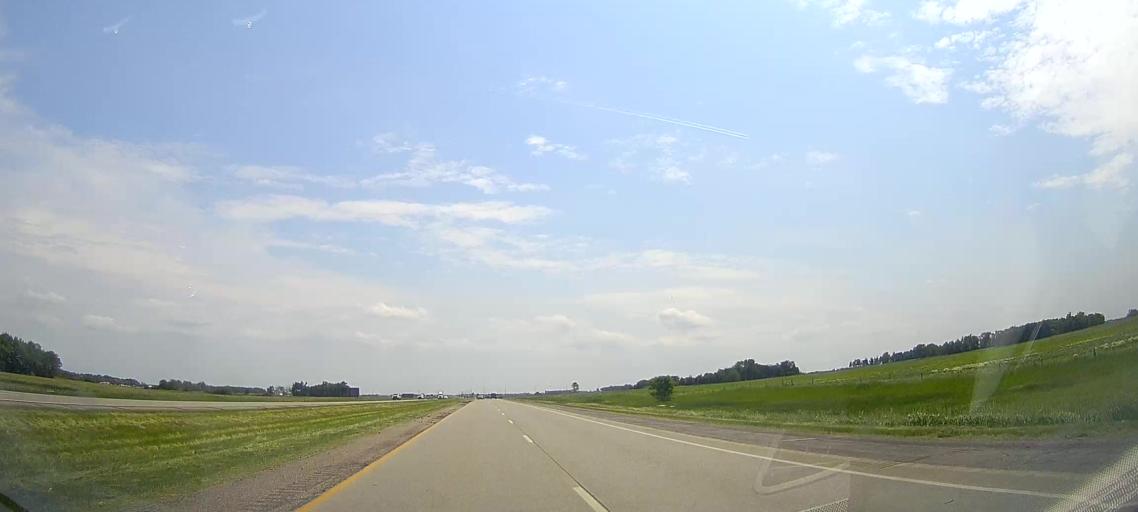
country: US
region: South Dakota
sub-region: Lincoln County
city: Tea
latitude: 43.4236
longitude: -96.7966
